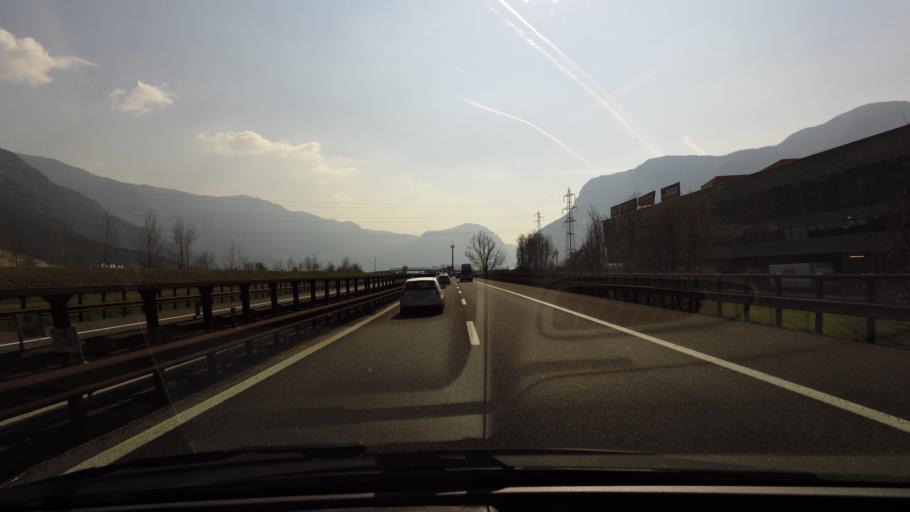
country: IT
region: Trentino-Alto Adige
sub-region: Bolzano
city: Laghetti
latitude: 46.2924
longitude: 11.2398
